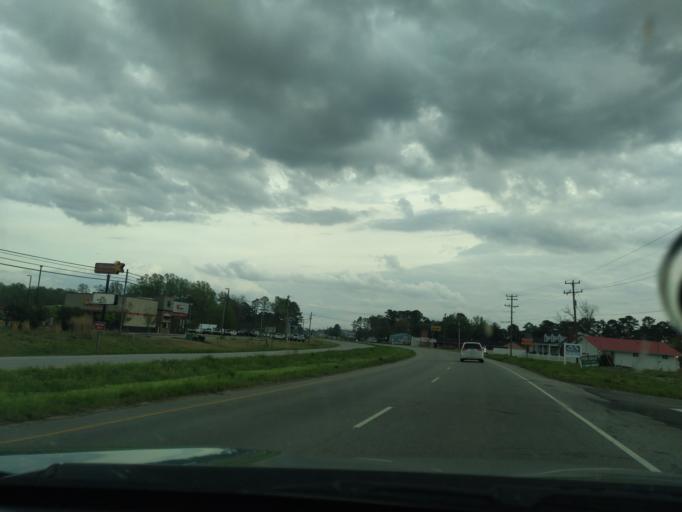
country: US
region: North Carolina
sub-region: Martin County
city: Williamston
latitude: 35.8339
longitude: -77.0669
